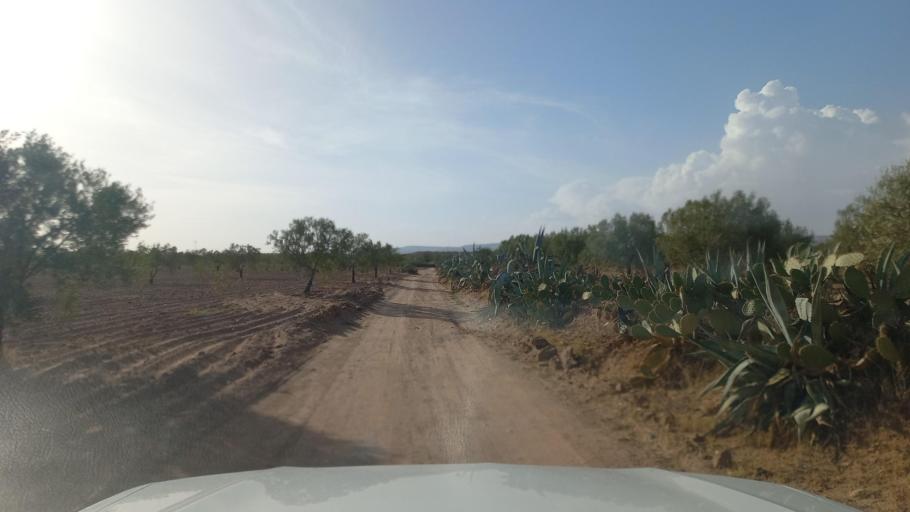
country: TN
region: Al Qasrayn
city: Kasserine
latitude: 35.2306
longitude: 8.9255
